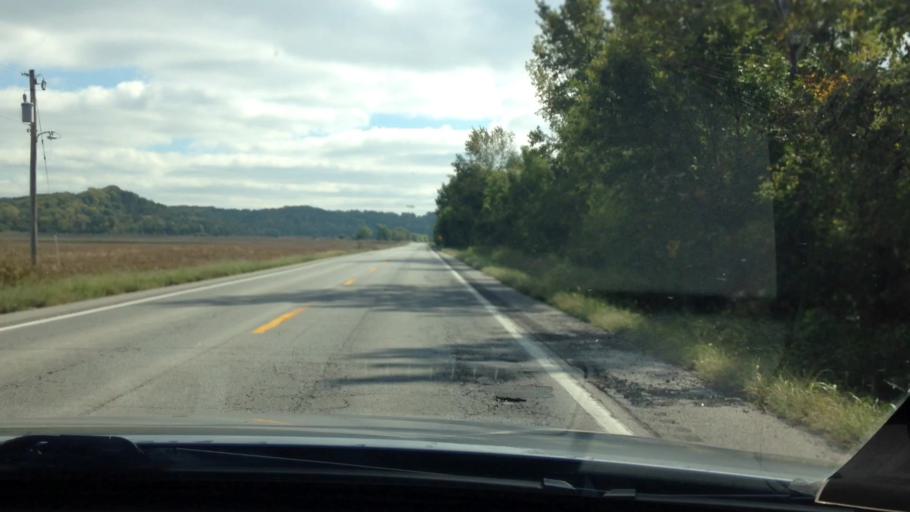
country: US
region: Kansas
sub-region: Leavenworth County
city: Lansing
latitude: 39.2663
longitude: -94.8184
